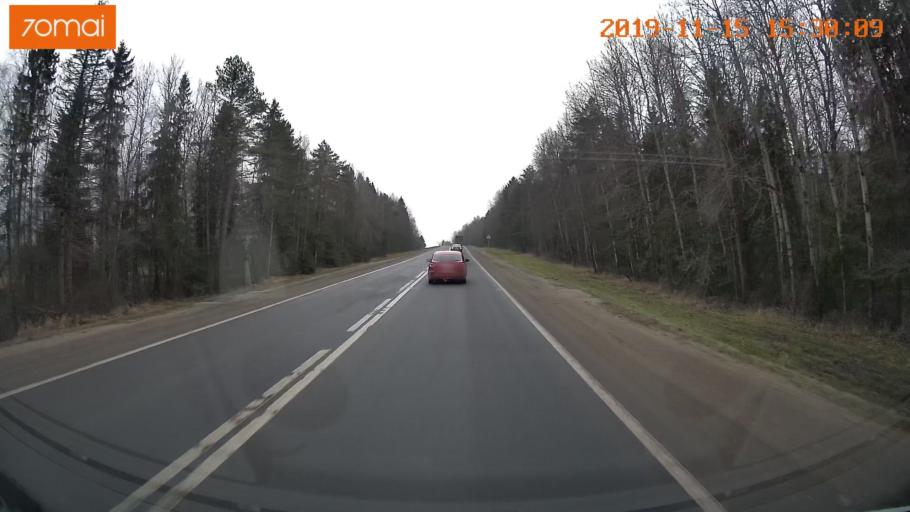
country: RU
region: Jaroslavl
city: Danilov
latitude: 58.1129
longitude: 40.1149
